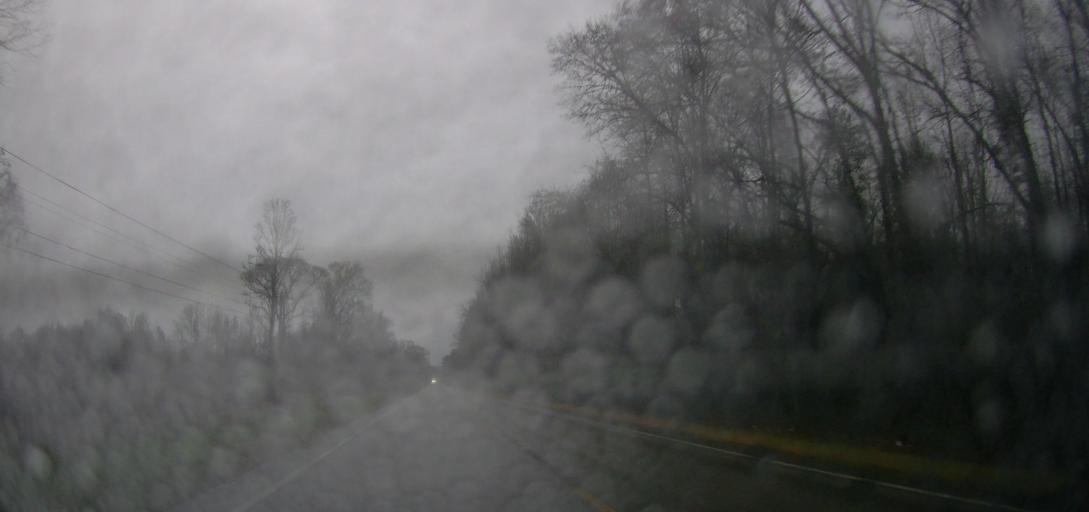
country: US
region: Alabama
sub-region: Autauga County
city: Prattville
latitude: 32.4834
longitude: -86.5347
